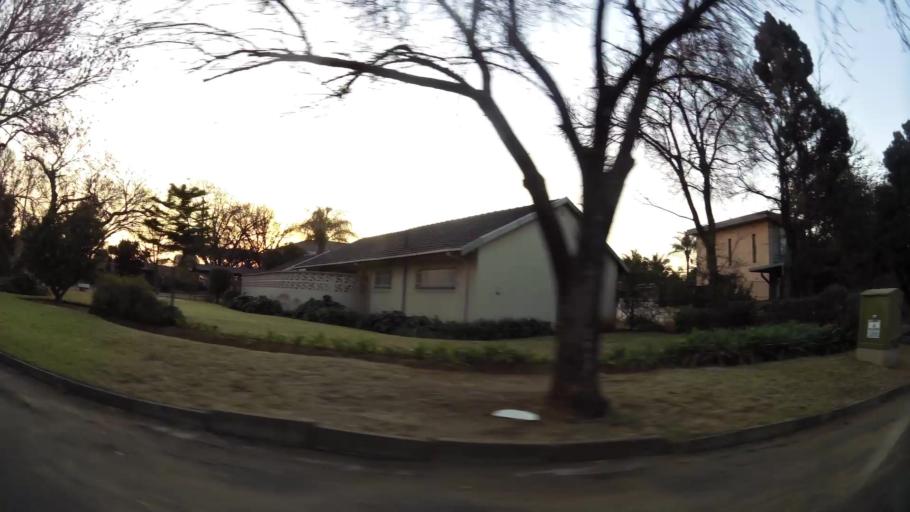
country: ZA
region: Gauteng
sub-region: Ekurhuleni Metropolitan Municipality
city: Tembisa
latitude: -26.0575
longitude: 28.2325
